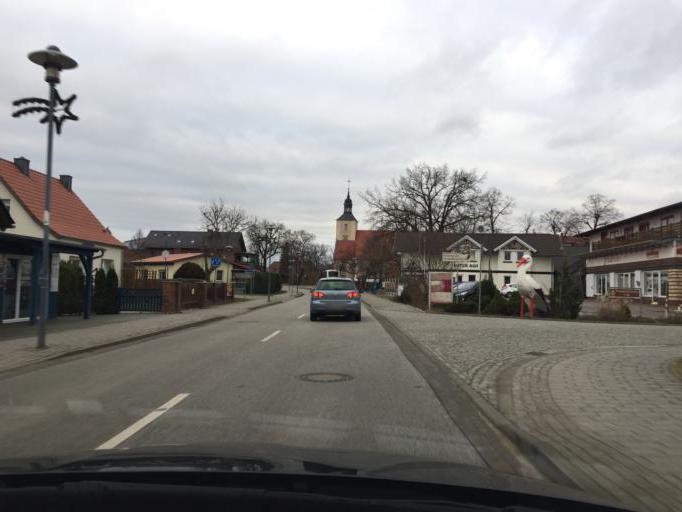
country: DE
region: Brandenburg
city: Burg
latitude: 51.8312
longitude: 14.1486
